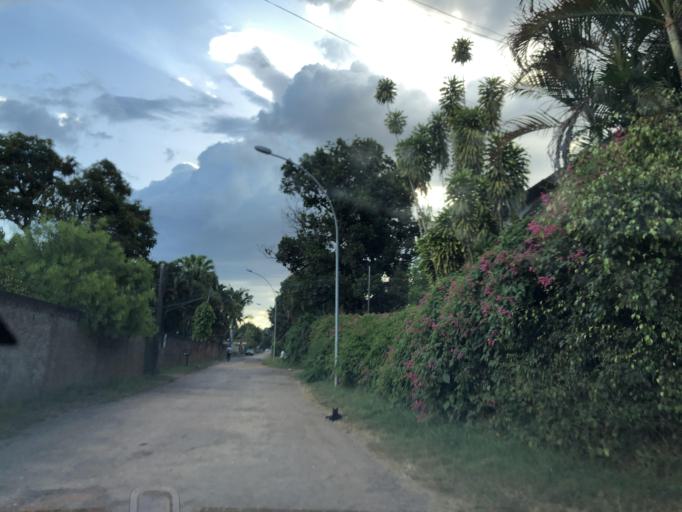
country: BR
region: Federal District
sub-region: Brasilia
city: Brasilia
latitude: -15.8762
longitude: -47.9712
